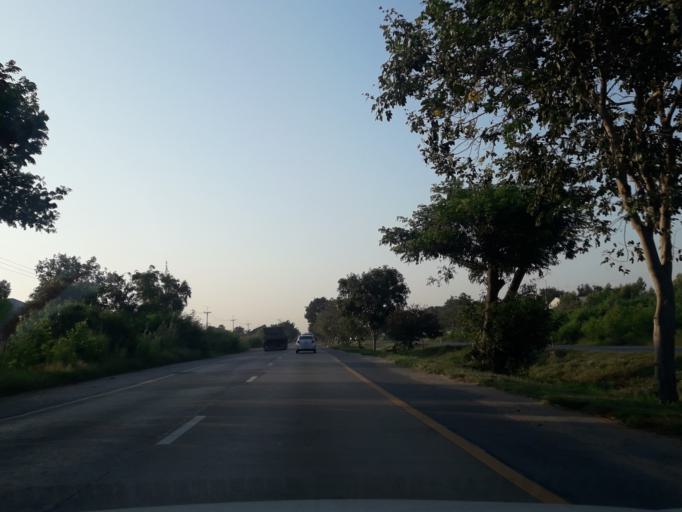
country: TH
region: Phra Nakhon Si Ayutthaya
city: Bang Pa-in
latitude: 14.2522
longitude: 100.5358
